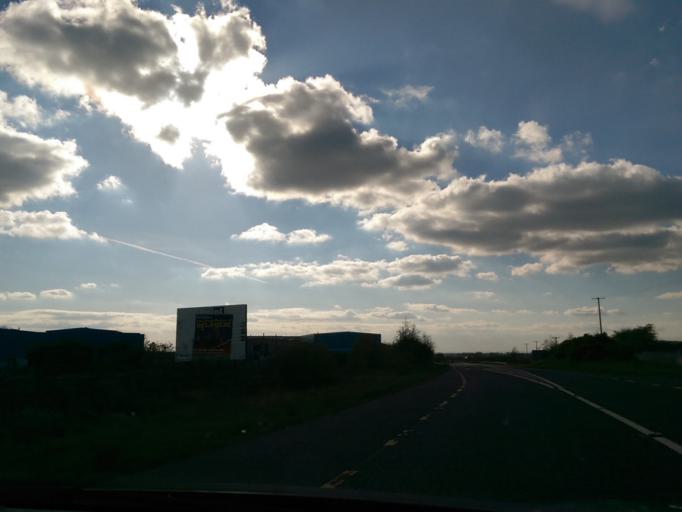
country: IE
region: Connaught
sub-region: County Galway
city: Loughrea
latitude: 53.2050
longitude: -8.5446
